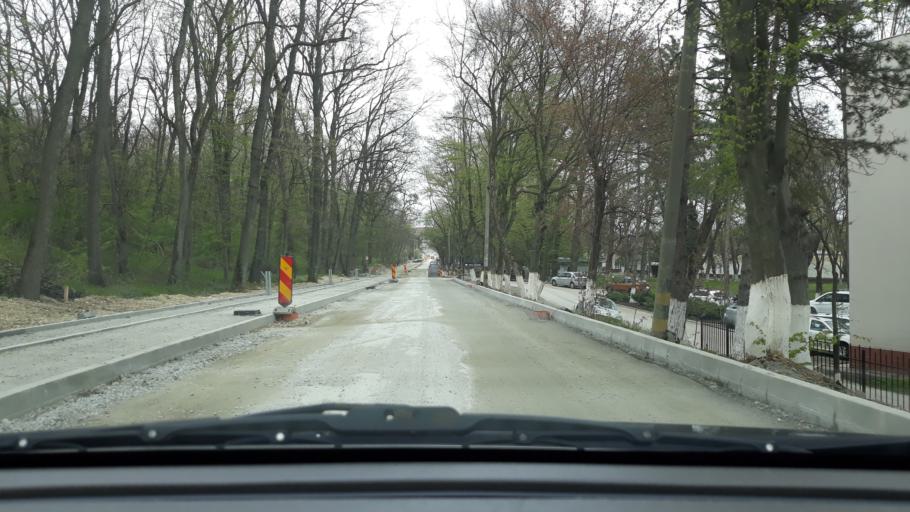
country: RO
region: Bihor
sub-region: Comuna Sanmartin
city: Sanmartin
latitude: 46.9924
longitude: 21.9768
